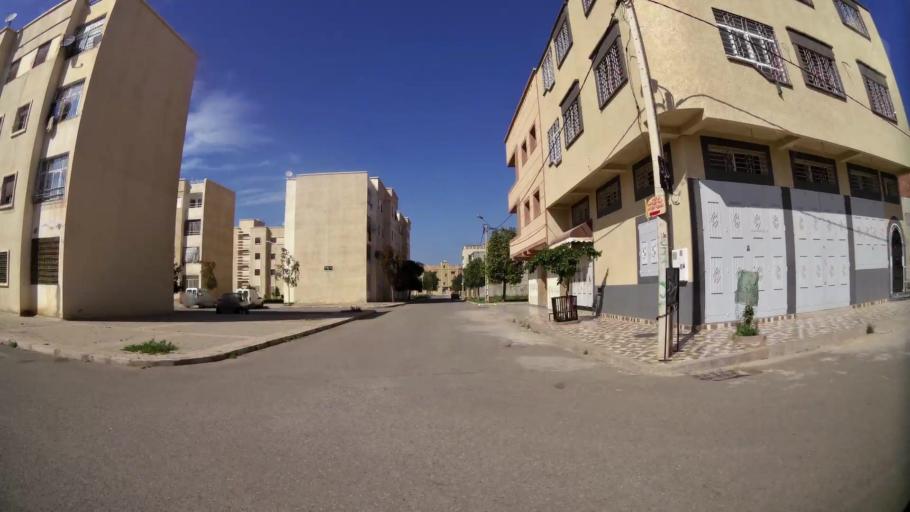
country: MA
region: Oriental
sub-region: Oujda-Angad
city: Oujda
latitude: 34.6980
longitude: -1.8802
